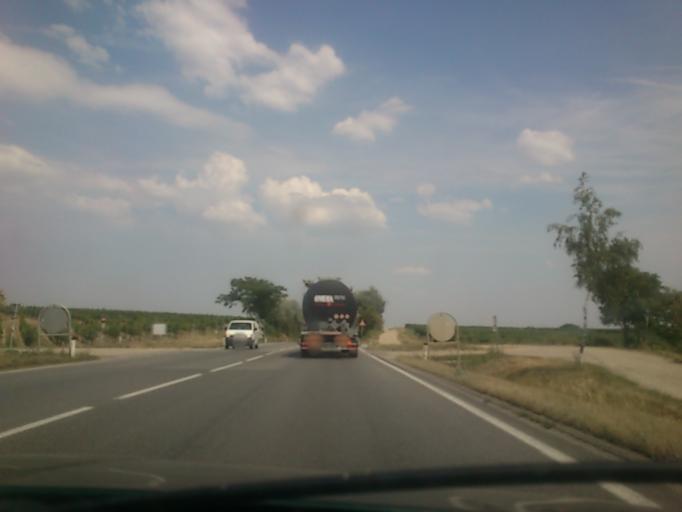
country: AT
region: Lower Austria
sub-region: Politischer Bezirk Mistelbach
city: Poysdorf
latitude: 48.6789
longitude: 16.6305
